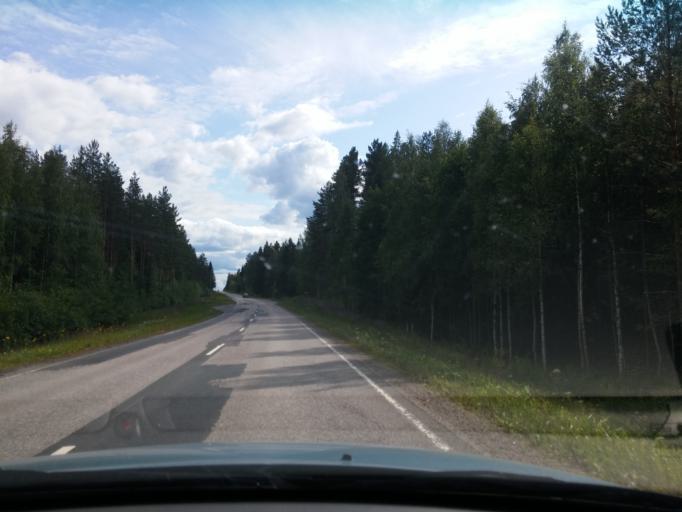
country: FI
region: Central Finland
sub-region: Keuruu
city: Keuruu
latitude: 62.3322
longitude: 24.7326
